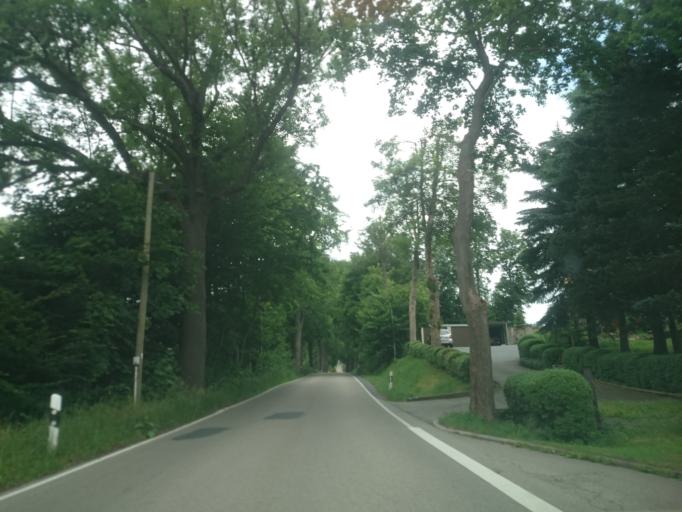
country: DE
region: Saxony
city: Eppendorf
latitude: 50.8140
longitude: 13.2569
